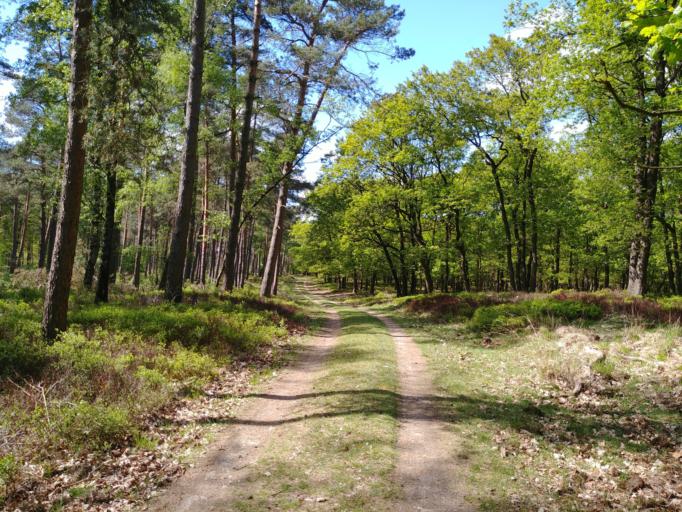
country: NL
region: Gelderland
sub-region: Gemeente Apeldoorn
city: Uddel
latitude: 52.2572
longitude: 5.8594
